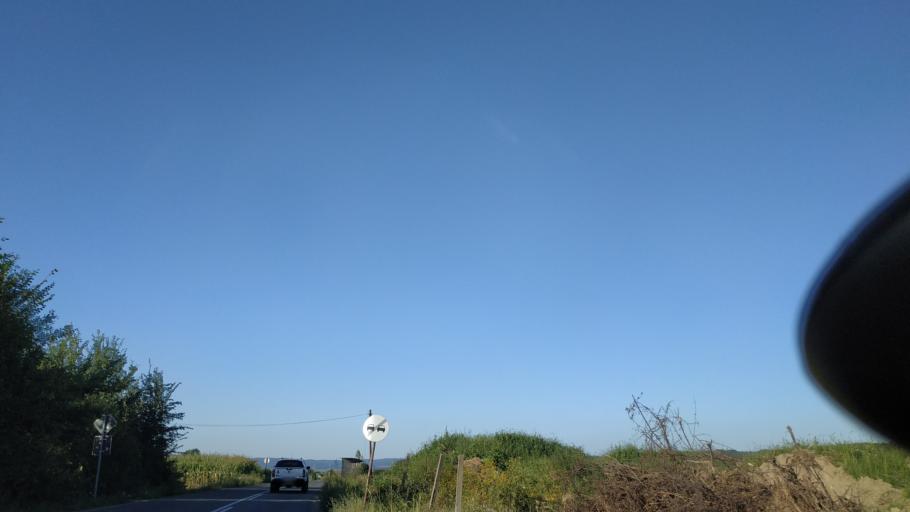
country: RS
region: Central Serbia
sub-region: Rasinski Okrug
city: Krusevac
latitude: 43.5155
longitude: 21.3274
